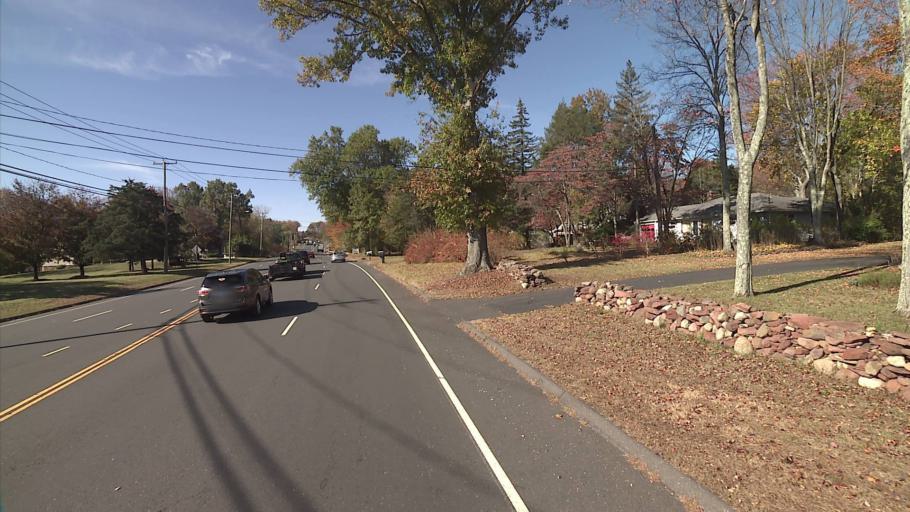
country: US
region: Connecticut
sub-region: Hartford County
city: Plainville
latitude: 41.7072
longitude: -72.8747
